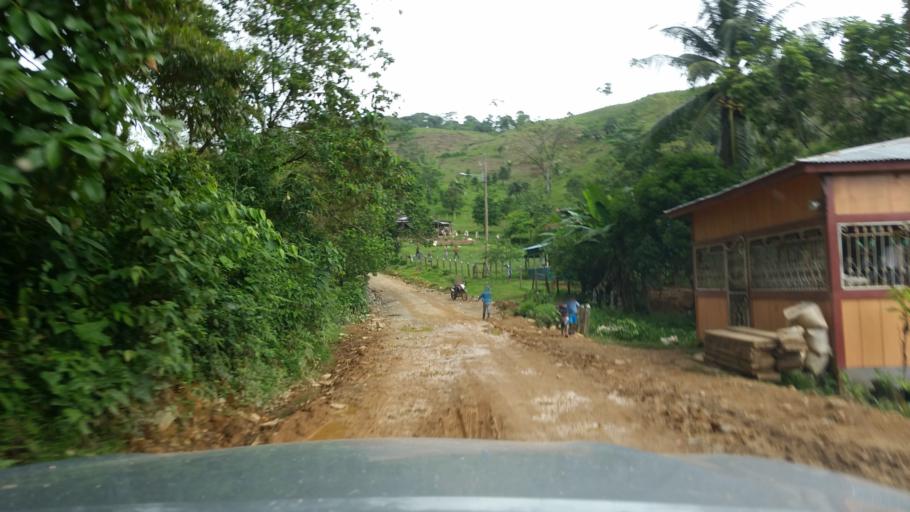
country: NI
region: Atlantico Norte (RAAN)
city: Bonanza
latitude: 13.9759
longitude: -84.6963
